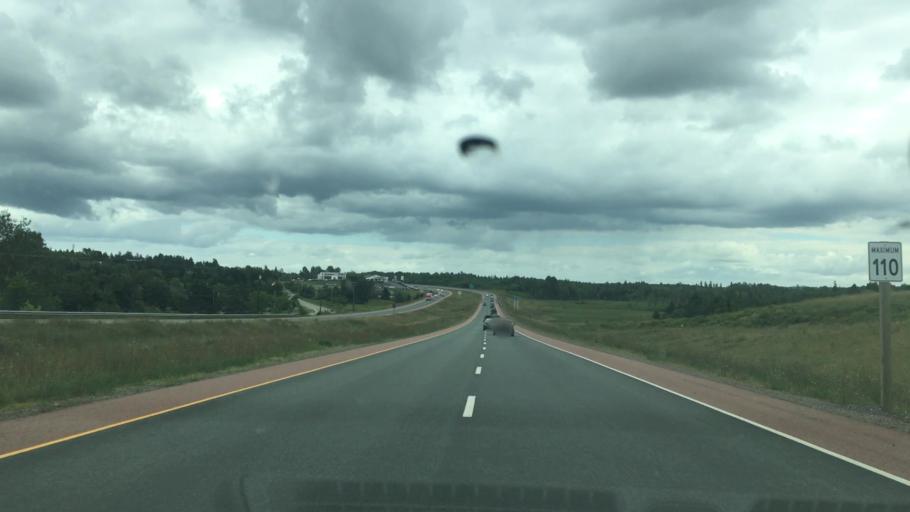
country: CA
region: Nova Scotia
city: Antigonish
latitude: 45.5968
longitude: -62.0426
